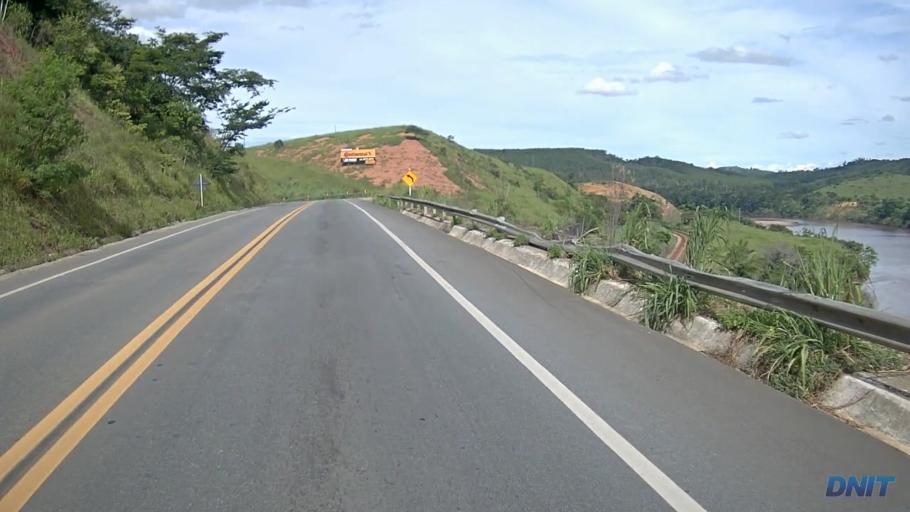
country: BR
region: Minas Gerais
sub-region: Belo Oriente
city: Belo Oriente
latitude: -19.2650
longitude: -42.3498
